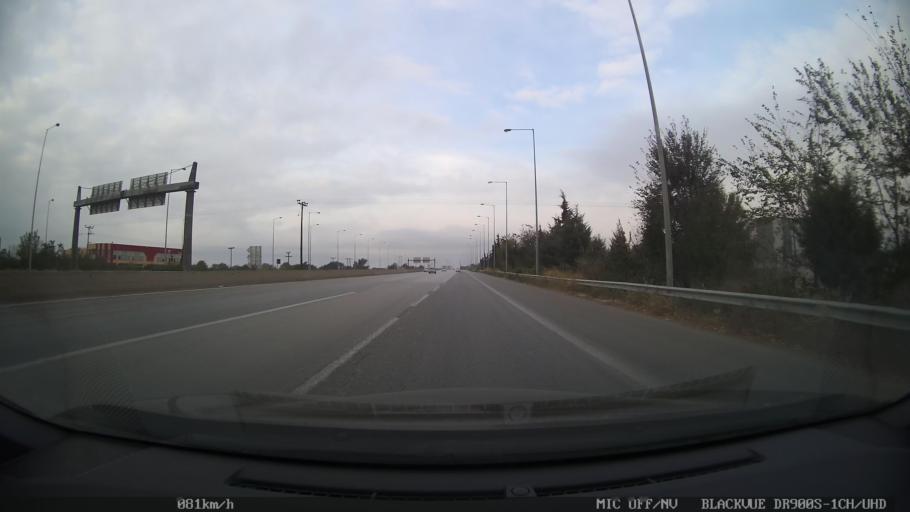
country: GR
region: Central Macedonia
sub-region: Nomos Thessalonikis
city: Kalochori
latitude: 40.6533
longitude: 22.8401
